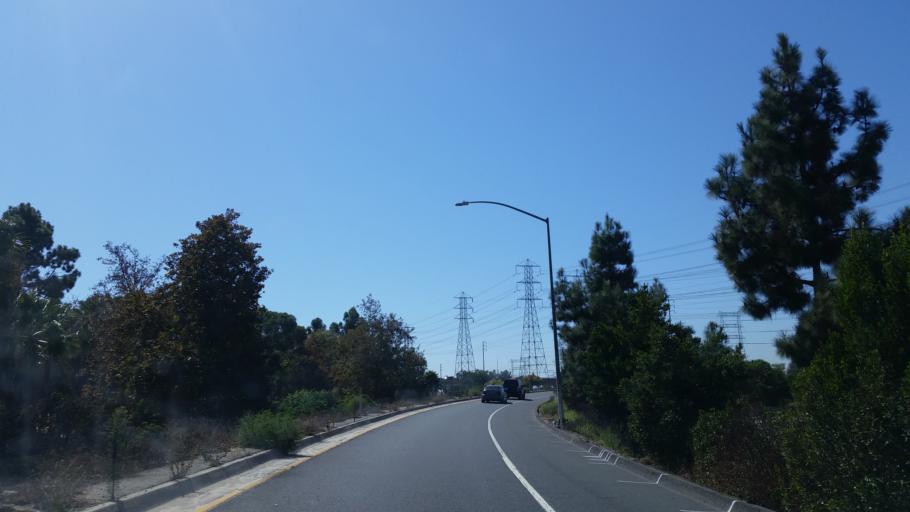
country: US
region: California
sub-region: Orange County
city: Rossmoor
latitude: 33.7876
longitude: -118.0906
